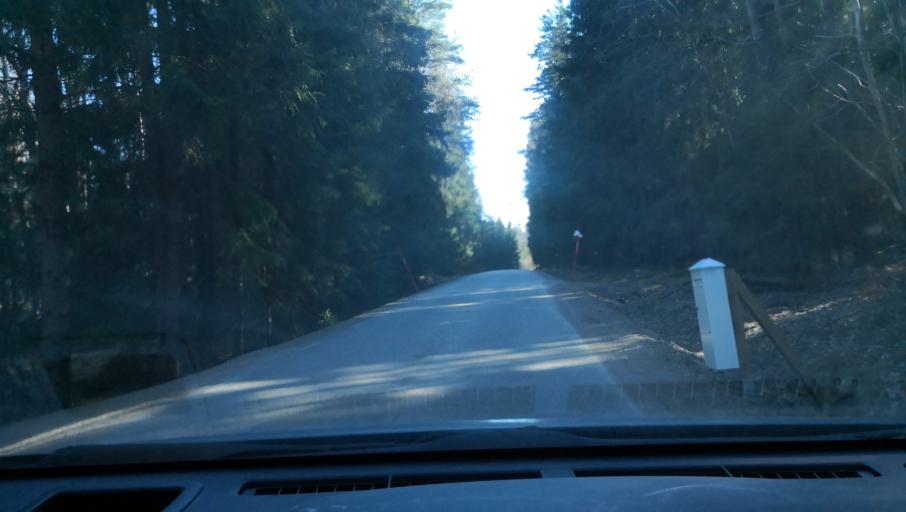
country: SE
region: Dalarna
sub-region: Avesta Kommun
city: Horndal
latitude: 60.0828
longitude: 16.3964
